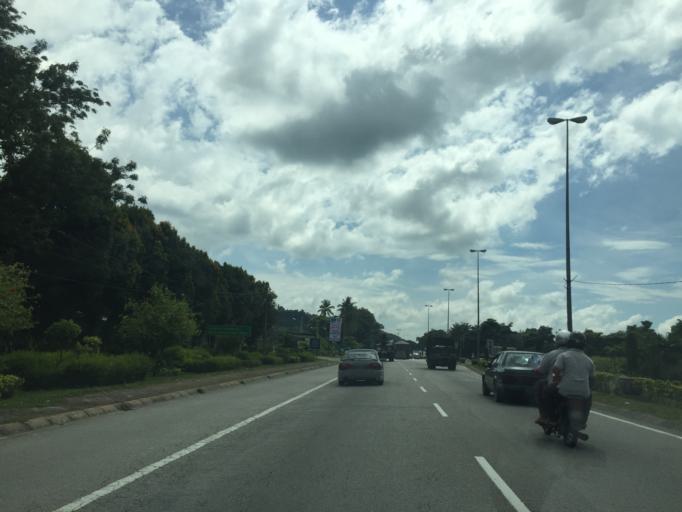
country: MY
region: Perak
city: Kampar
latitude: 4.3022
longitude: 101.1580
